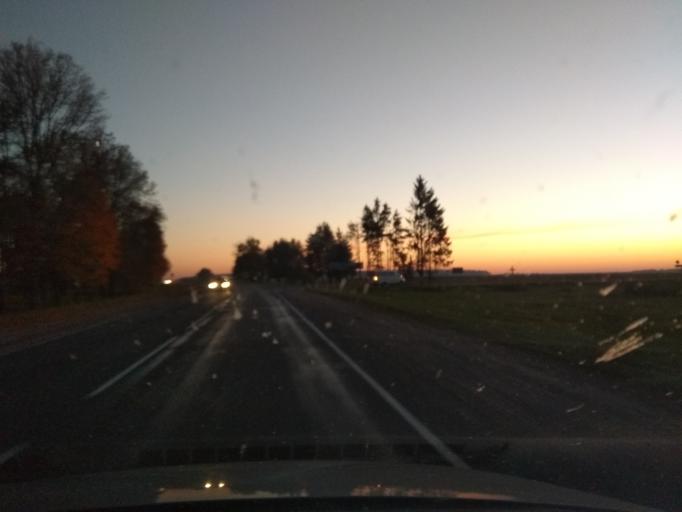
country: BY
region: Minsk
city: Dzyarzhynsk
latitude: 53.6554
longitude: 27.0774
